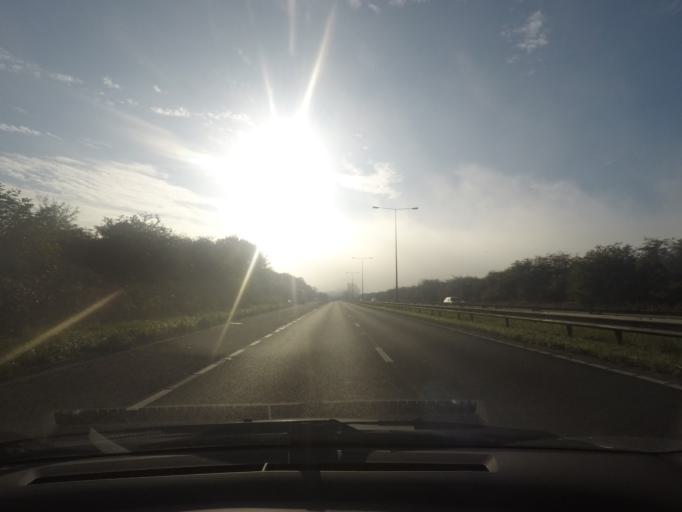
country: GB
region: England
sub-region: East Riding of Yorkshire
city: Welton
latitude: 53.7389
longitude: -0.5627
